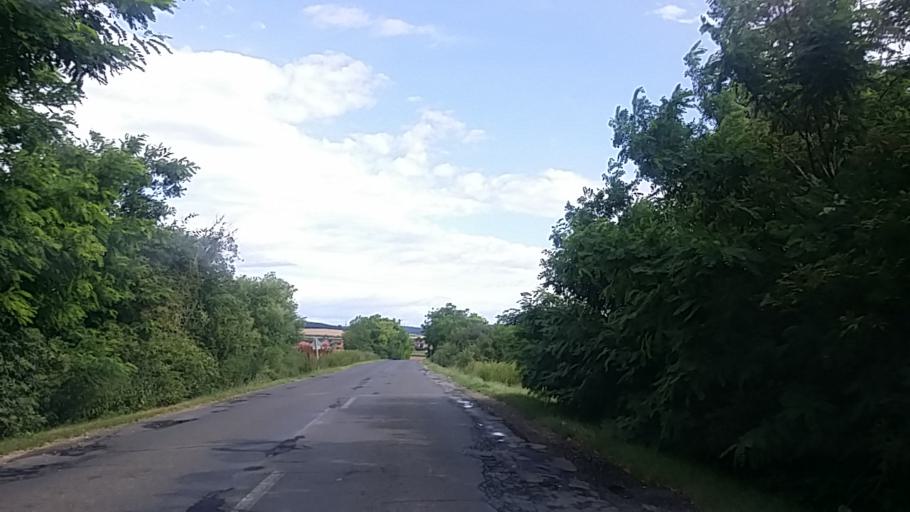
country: HU
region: Pest
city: Kosd
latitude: 47.7752
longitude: 19.2192
